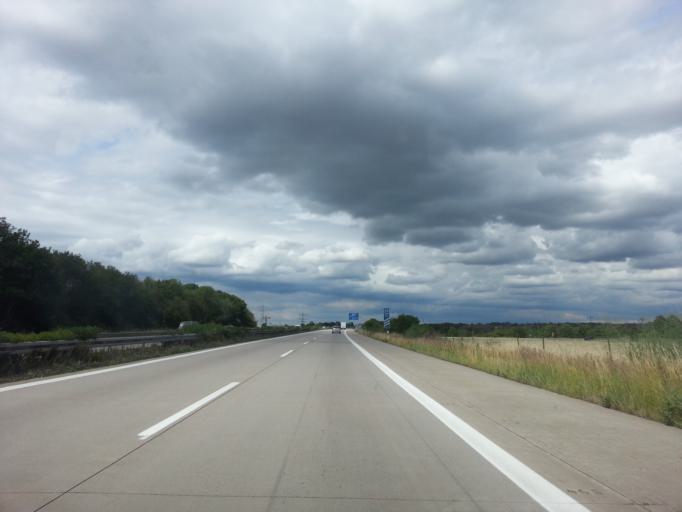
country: DE
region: Baden-Wuerttemberg
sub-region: Karlsruhe Region
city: Bruhl
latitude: 49.3992
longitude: 8.5447
